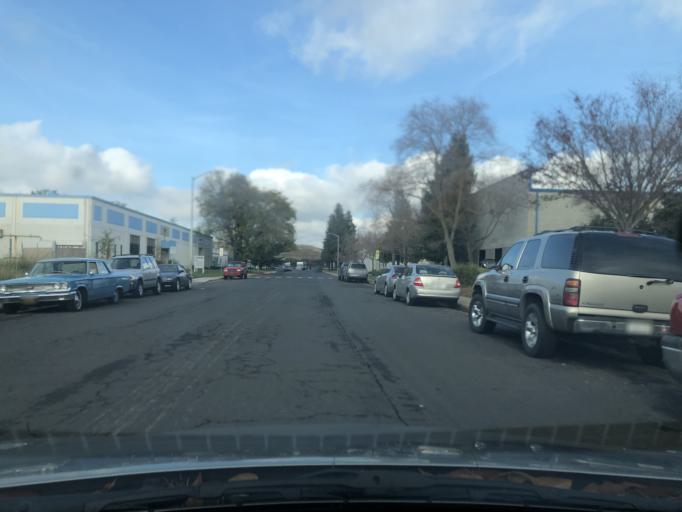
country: US
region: California
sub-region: Sacramento County
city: Rosemont
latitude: 38.5230
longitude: -121.3735
